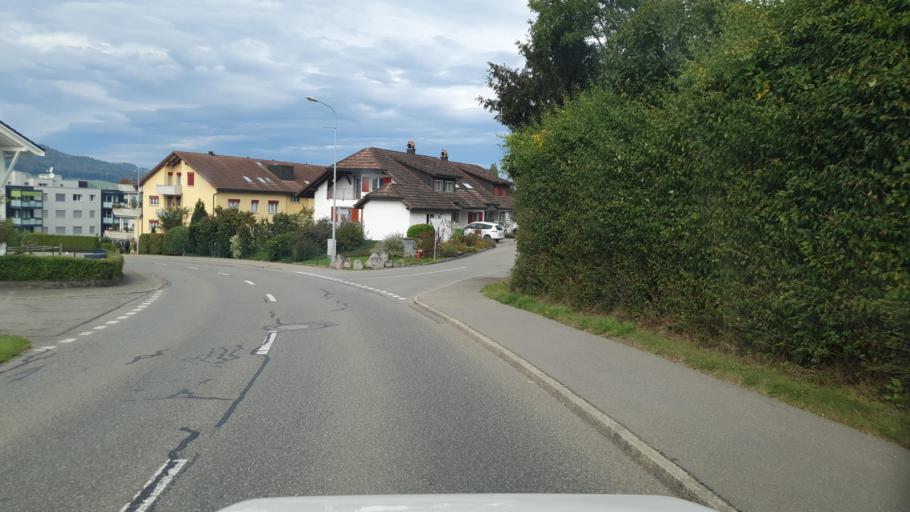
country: CH
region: Aargau
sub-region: Bezirk Lenzburg
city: Meisterschwanden
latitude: 47.2963
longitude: 8.2348
